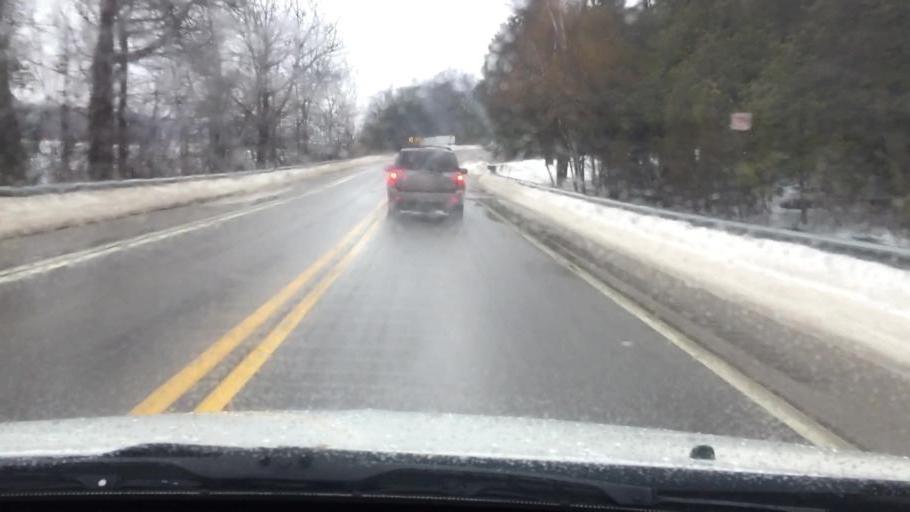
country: US
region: Michigan
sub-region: Charlevoix County
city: Charlevoix
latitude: 45.2498
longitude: -85.1826
